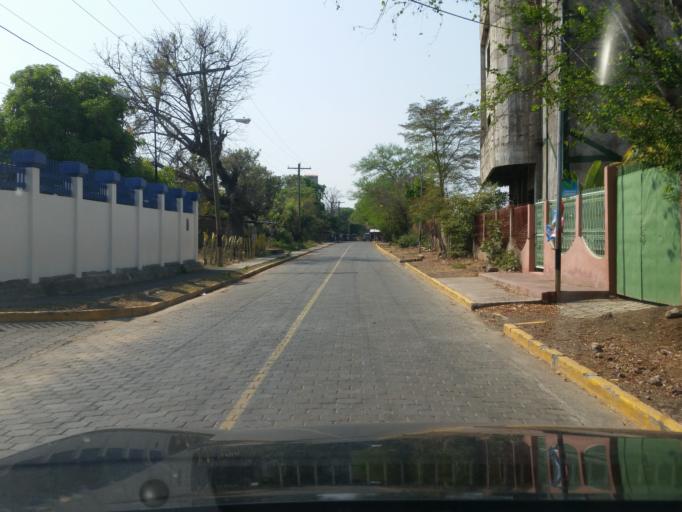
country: NI
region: Granada
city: Granada
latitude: 11.9365
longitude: -85.9752
